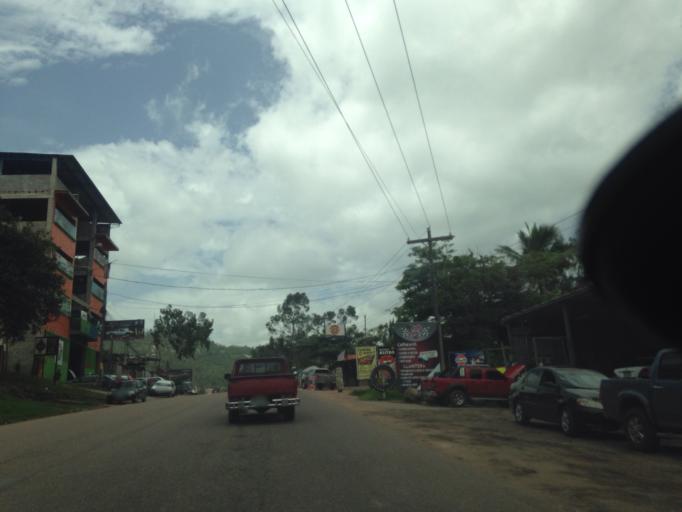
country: HN
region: Francisco Morazan
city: El Tablon
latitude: 14.0460
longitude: -87.1517
